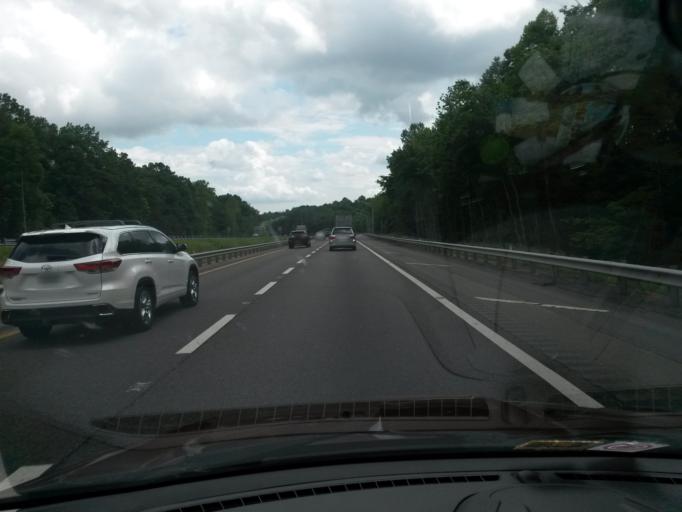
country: US
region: Virginia
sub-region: Carroll County
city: Cana
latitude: 36.5659
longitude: -80.7448
